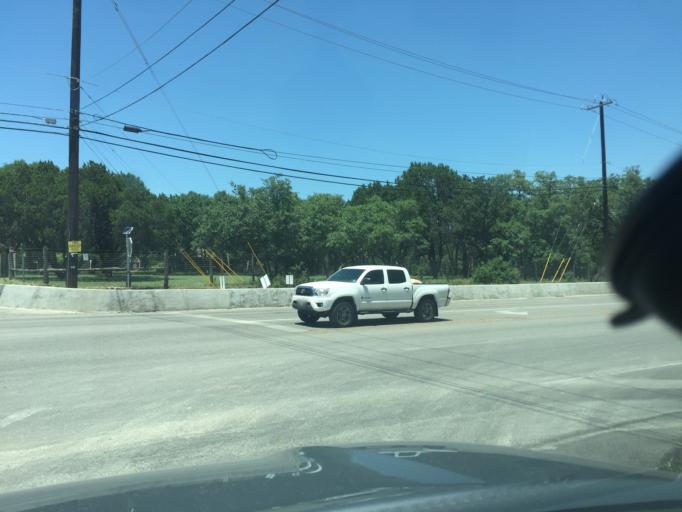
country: US
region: Texas
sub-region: Bexar County
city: Timberwood Park
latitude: 29.7096
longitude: -98.4840
